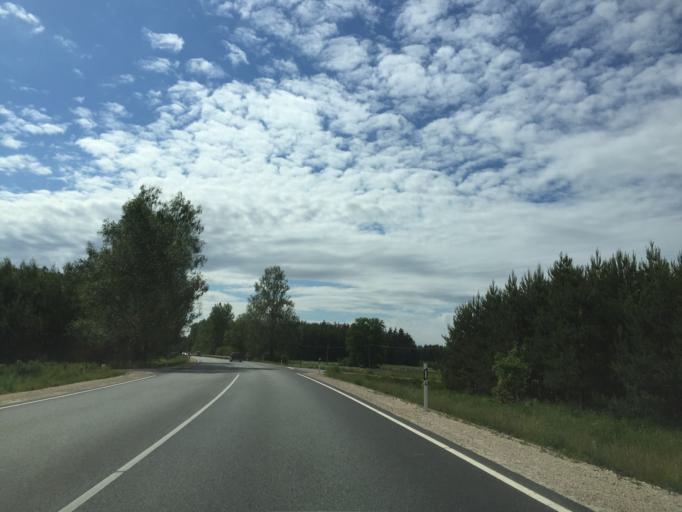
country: LV
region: Ikskile
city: Ikskile
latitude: 56.8924
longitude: 24.4686
